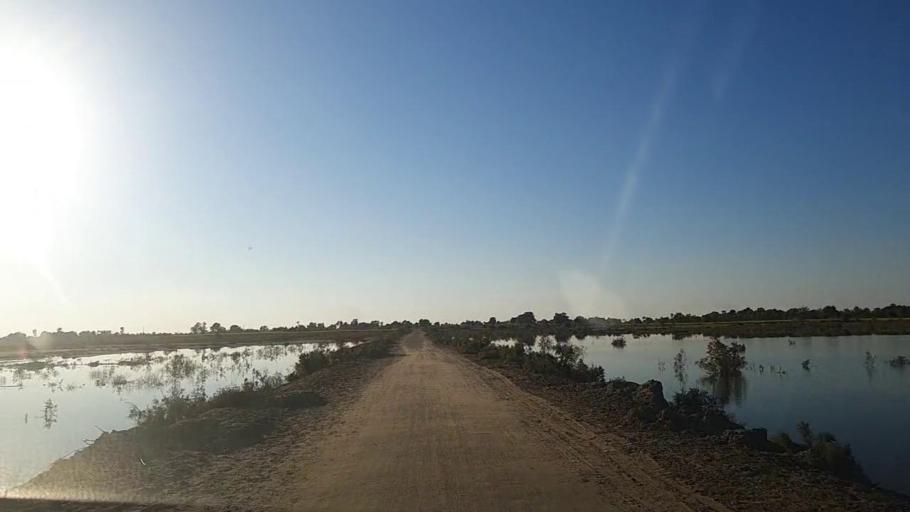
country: PK
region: Sindh
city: Sanghar
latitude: 26.1480
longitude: 68.9264
